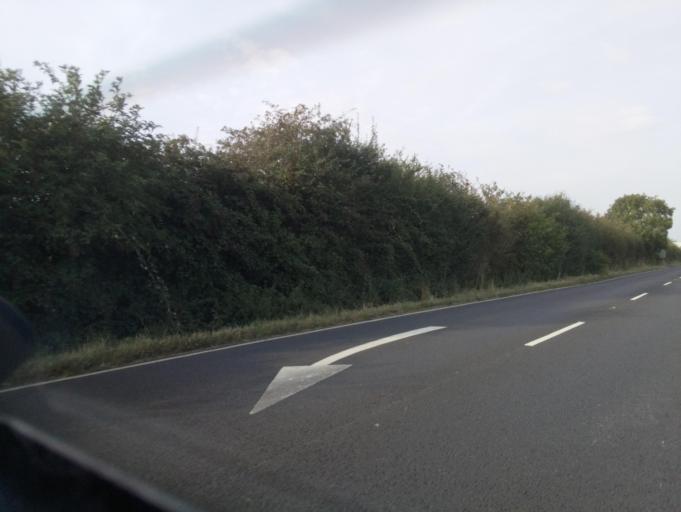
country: GB
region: England
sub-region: Gloucestershire
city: Gotherington
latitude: 52.0010
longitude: -2.0565
